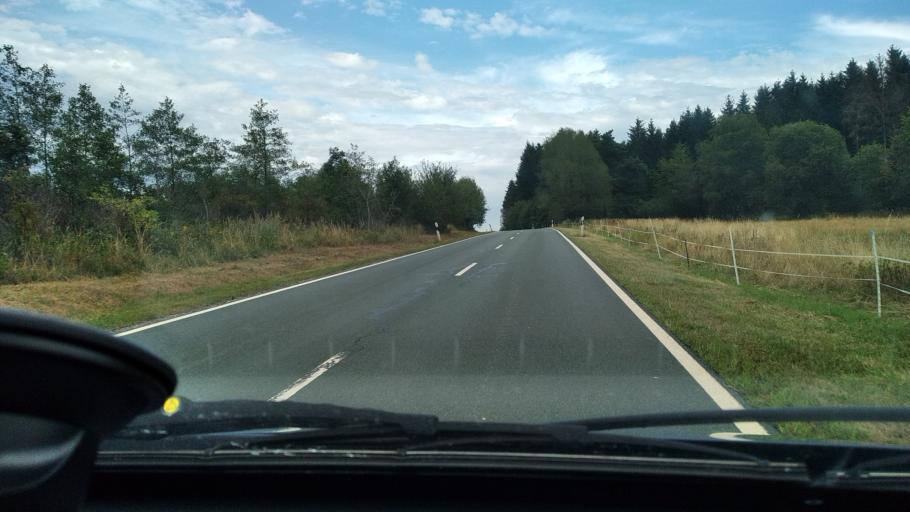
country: DE
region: Hesse
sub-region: Regierungsbezirk Giessen
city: Siegbach
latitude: 50.7891
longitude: 8.3716
